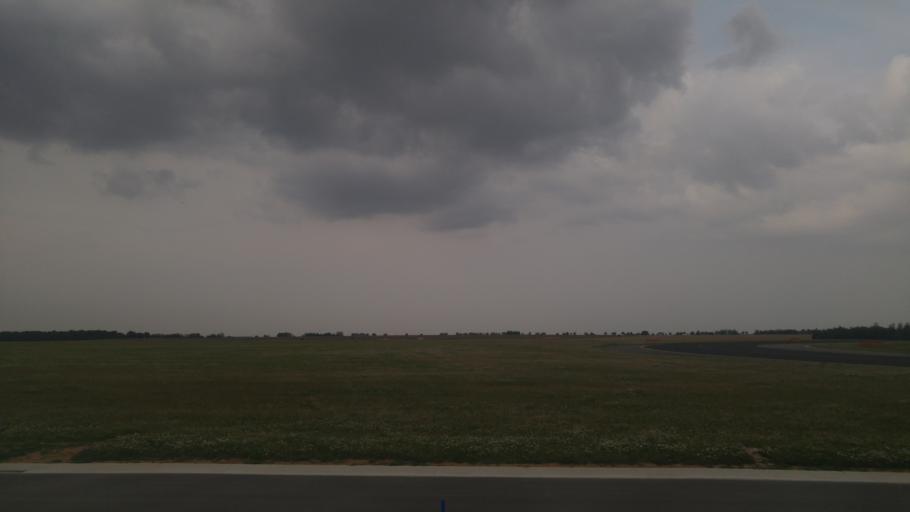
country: CZ
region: Central Bohemia
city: Hostivice
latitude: 50.1030
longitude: 14.2421
